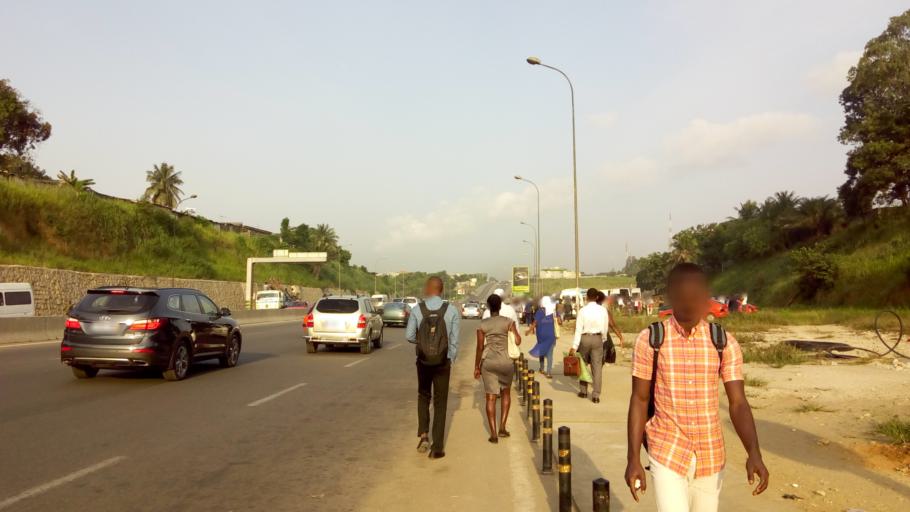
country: CI
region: Lagunes
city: Abidjan
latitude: 5.3530
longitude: -3.9798
